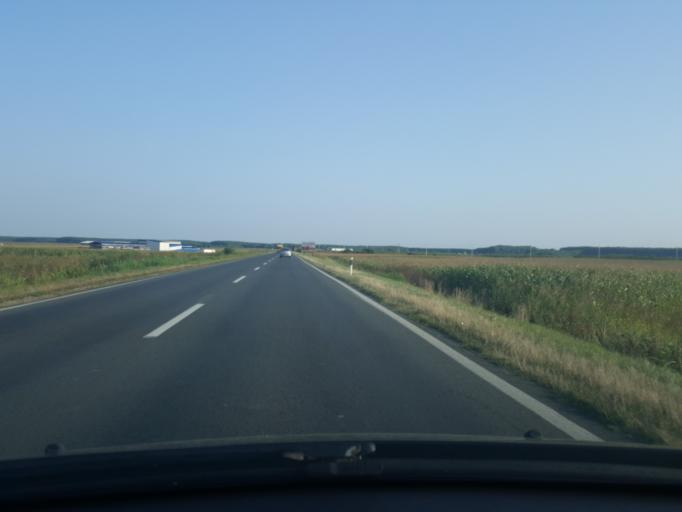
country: RS
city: Klenak
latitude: 44.7793
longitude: 19.7242
